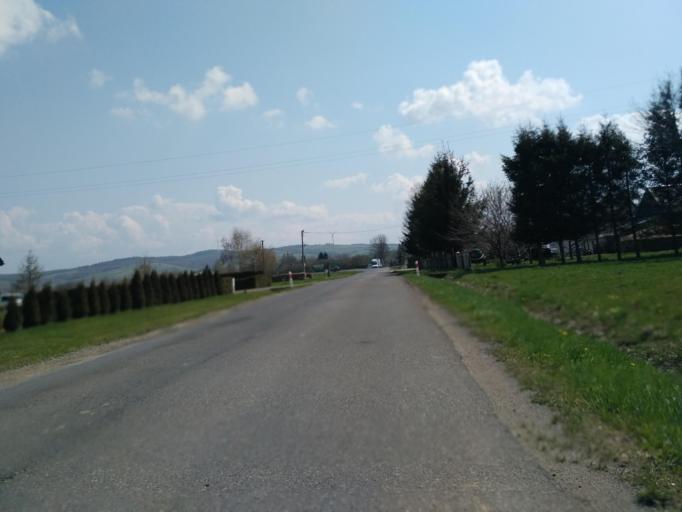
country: PL
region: Subcarpathian Voivodeship
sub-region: Powiat sanocki
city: Bukowsko
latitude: 49.5125
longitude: 22.0069
